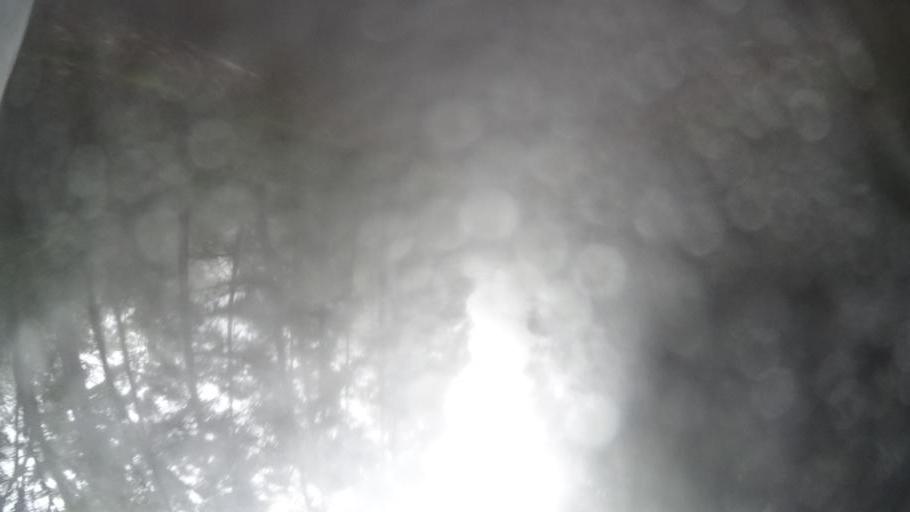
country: JP
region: Kagoshima
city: Nishinoomote
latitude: 30.2988
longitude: 130.5580
